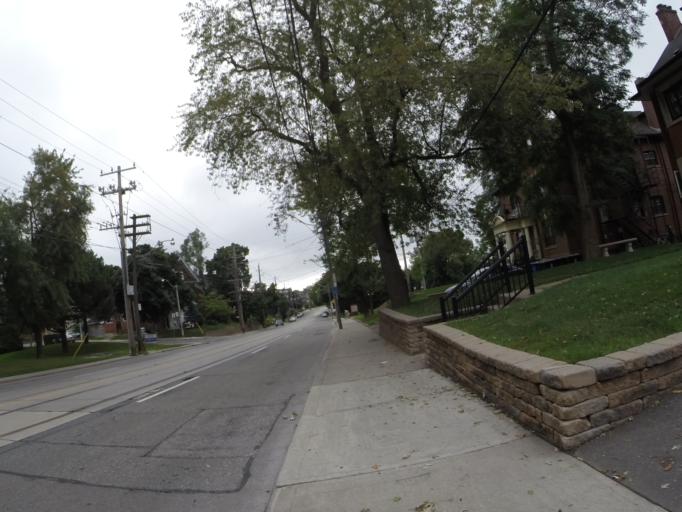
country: CA
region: Ontario
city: Toronto
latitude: 43.6747
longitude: -79.3575
